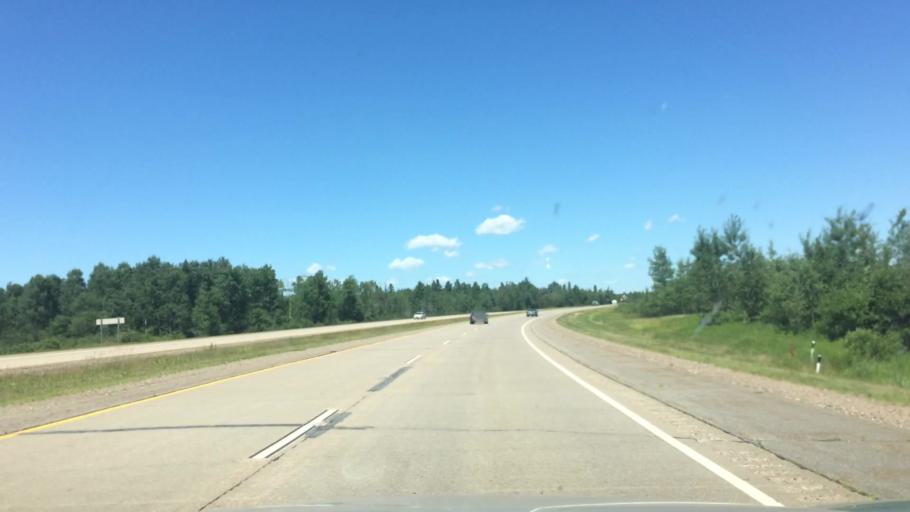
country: US
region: Wisconsin
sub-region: Lincoln County
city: Tomahawk
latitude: 45.3823
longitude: -89.6717
